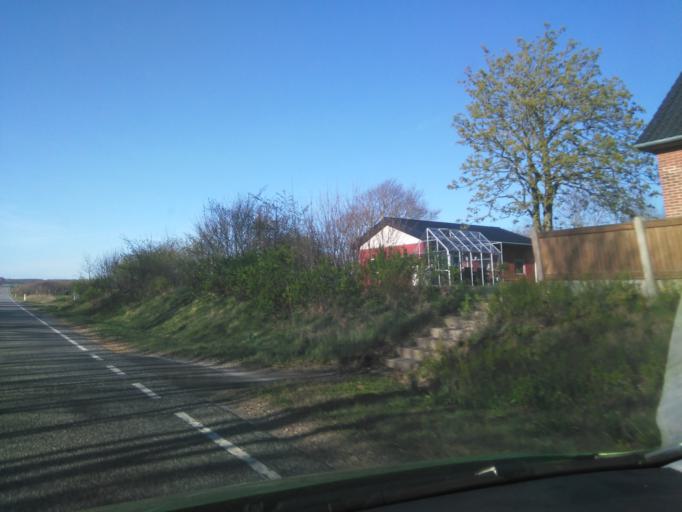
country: DK
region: Central Jutland
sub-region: Ringkobing-Skjern Kommune
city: Skjern
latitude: 56.0619
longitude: 8.5047
